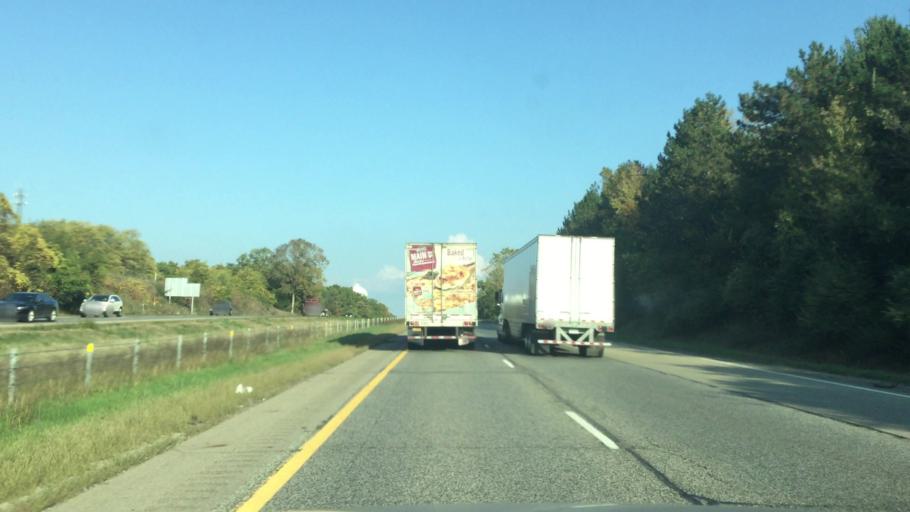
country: US
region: Michigan
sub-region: Washtenaw County
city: Chelsea
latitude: 42.2927
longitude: -84.0629
